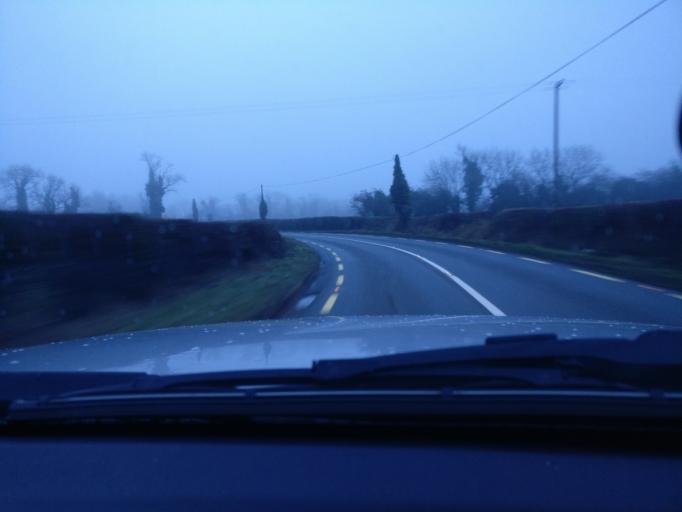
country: IE
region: Leinster
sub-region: An Mhi
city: Athboy
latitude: 53.6035
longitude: -6.9861
